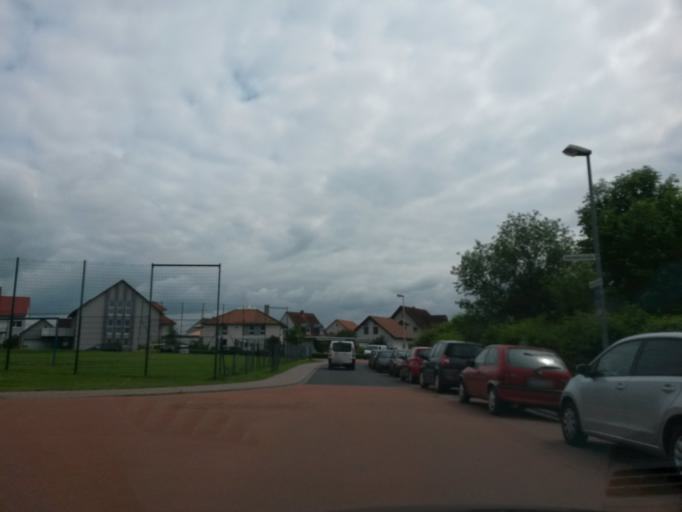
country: DE
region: Bavaria
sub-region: Regierungsbezirk Unterfranken
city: Rimpar
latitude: 49.8538
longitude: 9.9659
